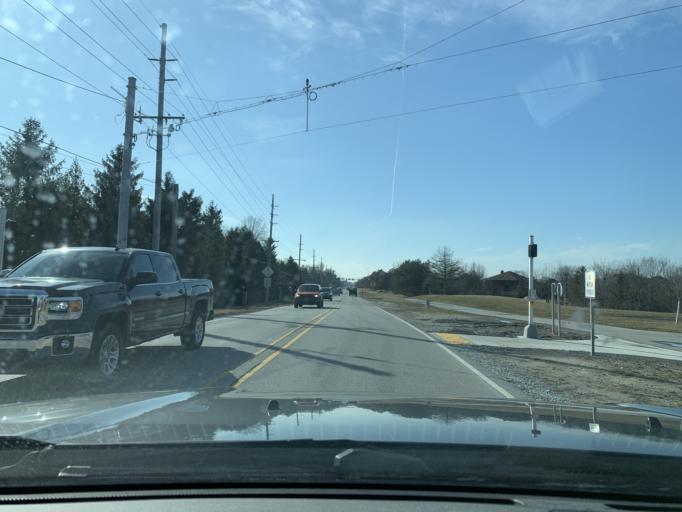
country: US
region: Indiana
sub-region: Lake County
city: Dyer
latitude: 41.5232
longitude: -87.4906
